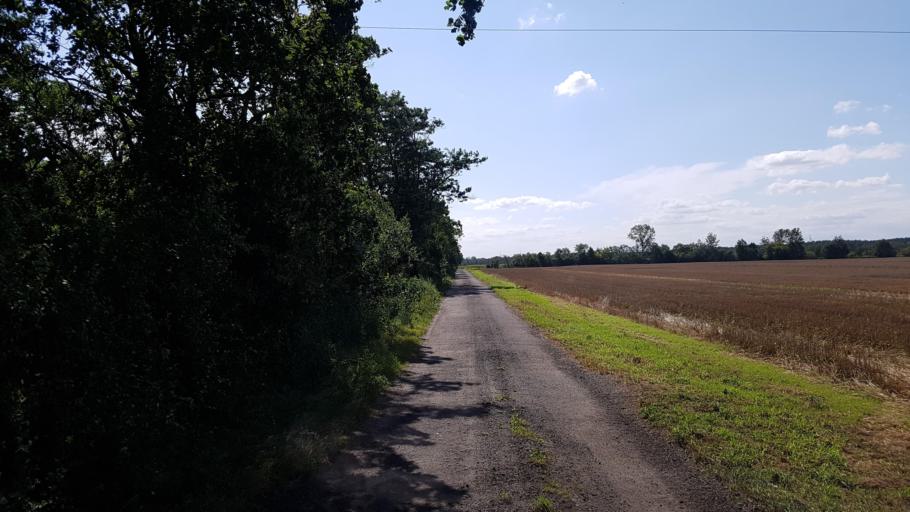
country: DE
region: Brandenburg
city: Bad Liebenwerda
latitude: 51.5136
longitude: 13.3371
